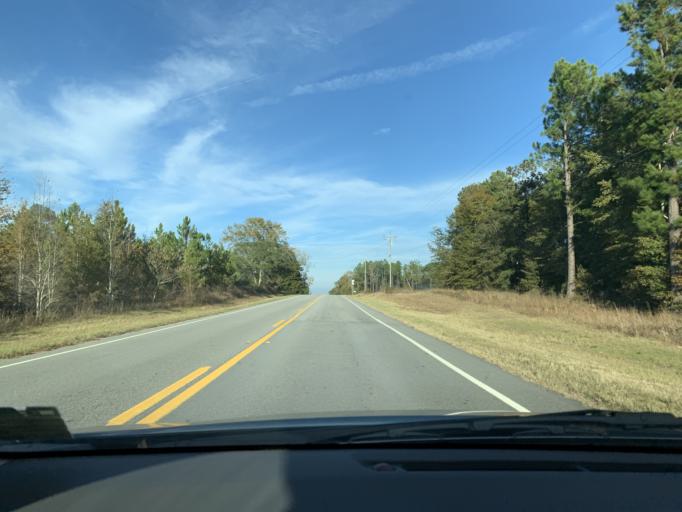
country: US
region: Georgia
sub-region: Irwin County
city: Ocilla
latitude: 31.6239
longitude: -83.4252
